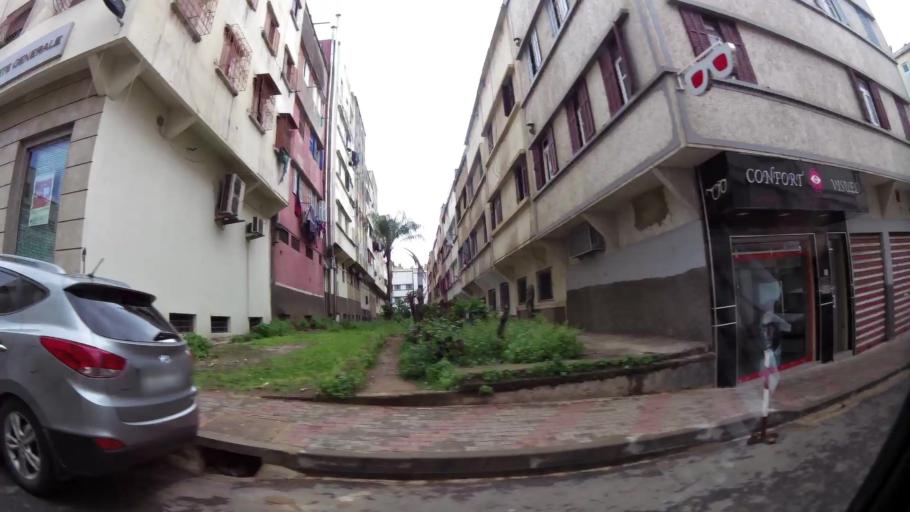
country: MA
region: Grand Casablanca
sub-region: Casablanca
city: Casablanca
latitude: 33.5398
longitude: -7.5752
